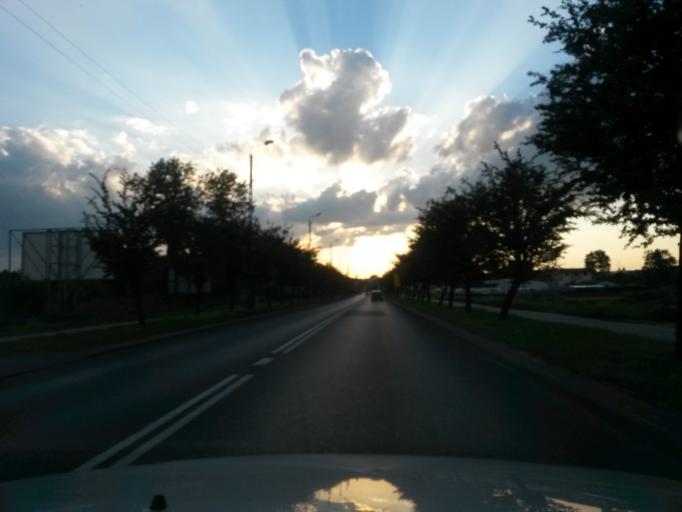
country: PL
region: Lodz Voivodeship
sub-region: Powiat wielunski
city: Wielun
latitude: 51.2235
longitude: 18.5732
